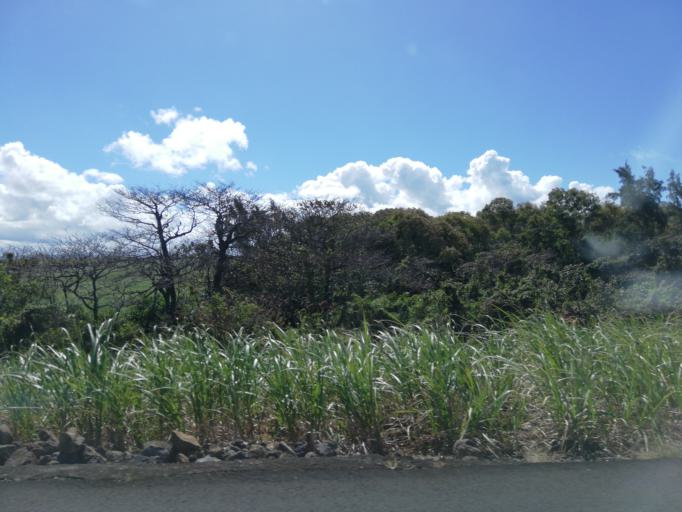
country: MU
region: Grand Port
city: Beau Vallon
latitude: -20.4476
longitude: 57.6978
